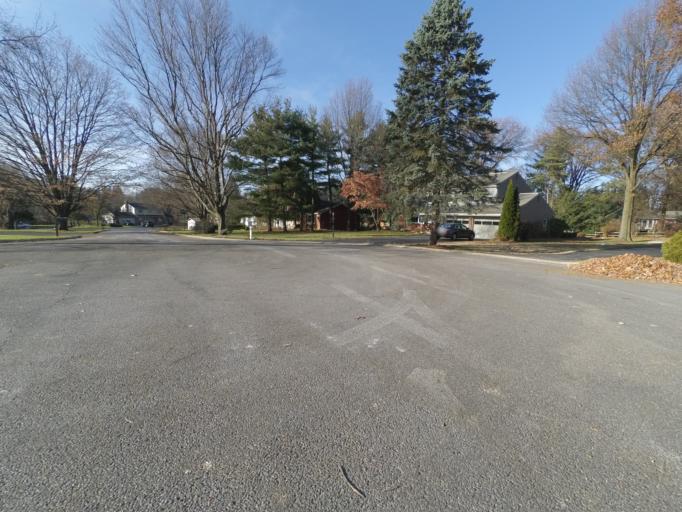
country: US
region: Pennsylvania
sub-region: Centre County
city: Lemont
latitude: 40.7950
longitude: -77.8297
